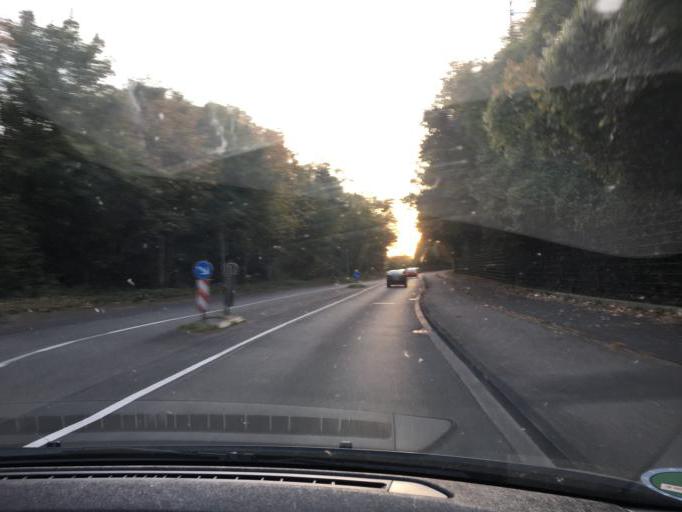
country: DE
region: North Rhine-Westphalia
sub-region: Regierungsbezirk Koln
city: Hurth
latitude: 50.8616
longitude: 6.8581
